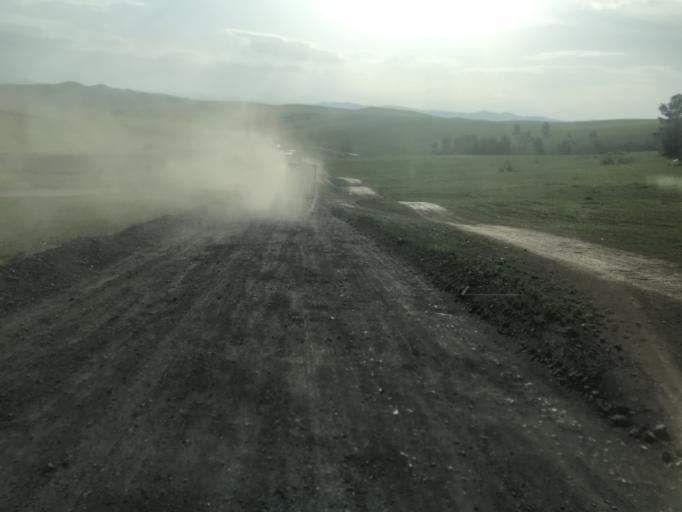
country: MN
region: Central Aimak
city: Javhlant
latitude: 48.6497
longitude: 106.0981
